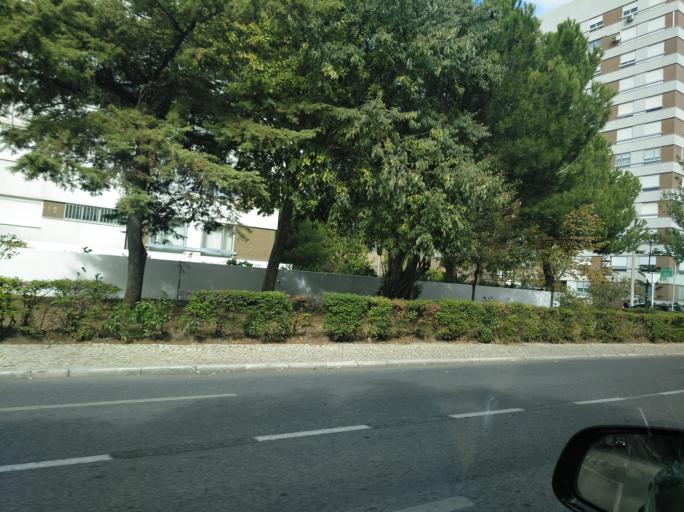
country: PT
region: Lisbon
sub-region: Loures
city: Sacavem
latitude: 38.7836
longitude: -9.1137
